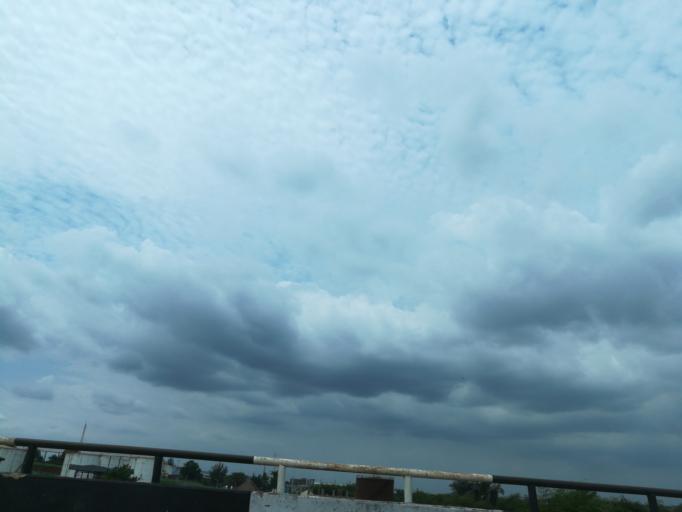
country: NG
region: Lagos
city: Oshodi
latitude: 6.5598
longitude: 3.3246
